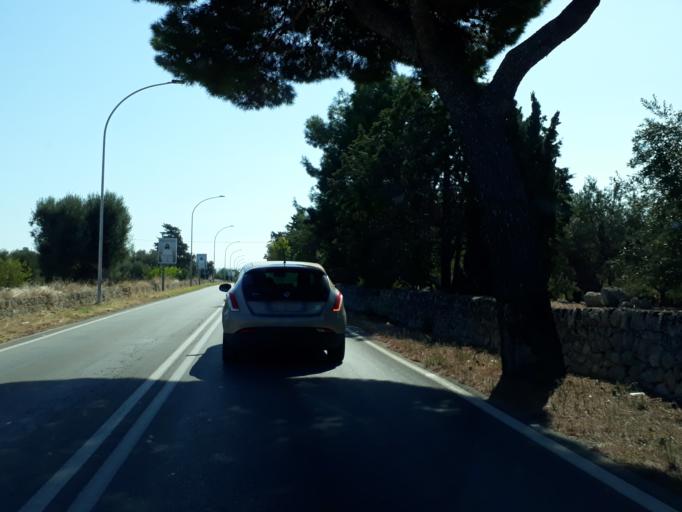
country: IT
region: Apulia
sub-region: Provincia di Bari
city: Monopoli
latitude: 40.9305
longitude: 17.3120
